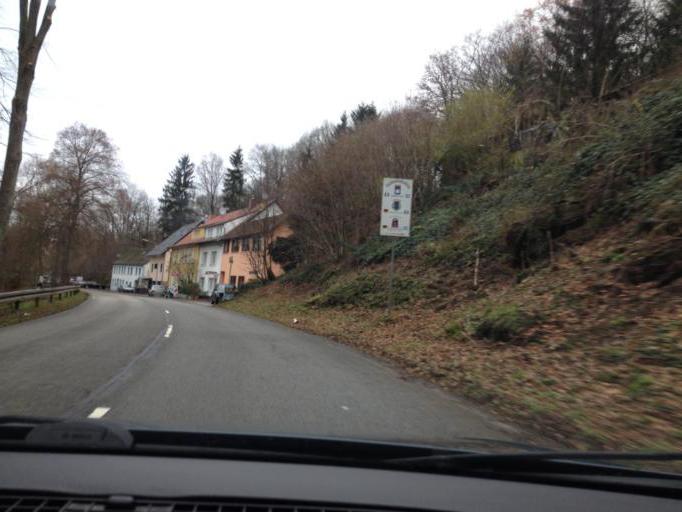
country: DE
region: Rheinland-Pfalz
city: Breitenbach
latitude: 49.4154
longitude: 7.2355
